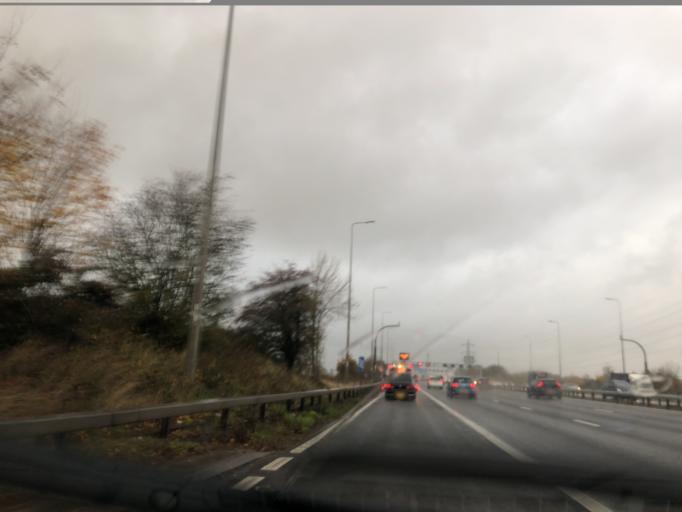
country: GB
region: England
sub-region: Solihull
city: Bickenhill
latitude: 52.4340
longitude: -1.7159
